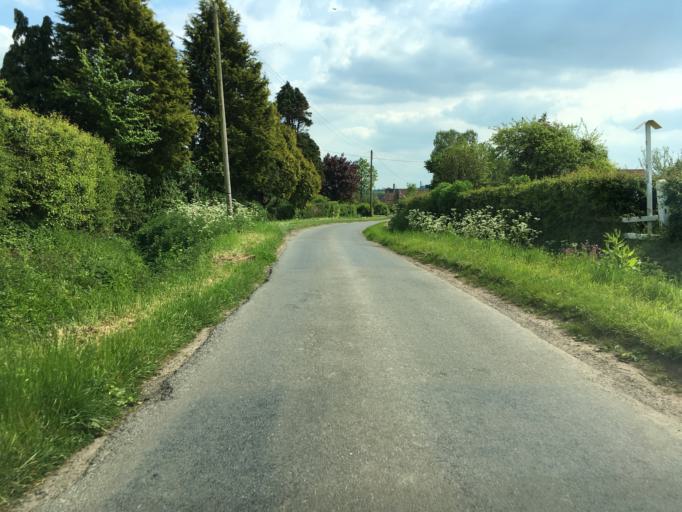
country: GB
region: England
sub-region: South Gloucestershire
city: Thornbury
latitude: 51.6206
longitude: -2.5478
